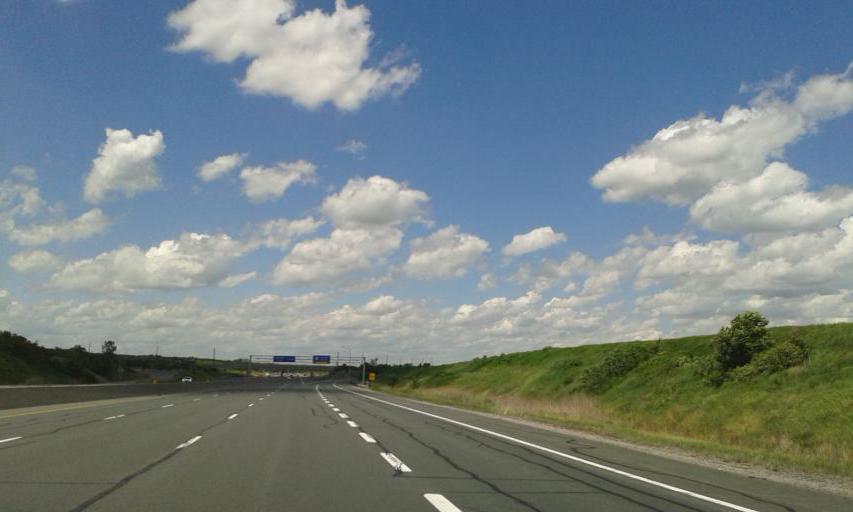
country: CA
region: Ontario
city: Burlington
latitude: 43.3771
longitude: -79.8327
